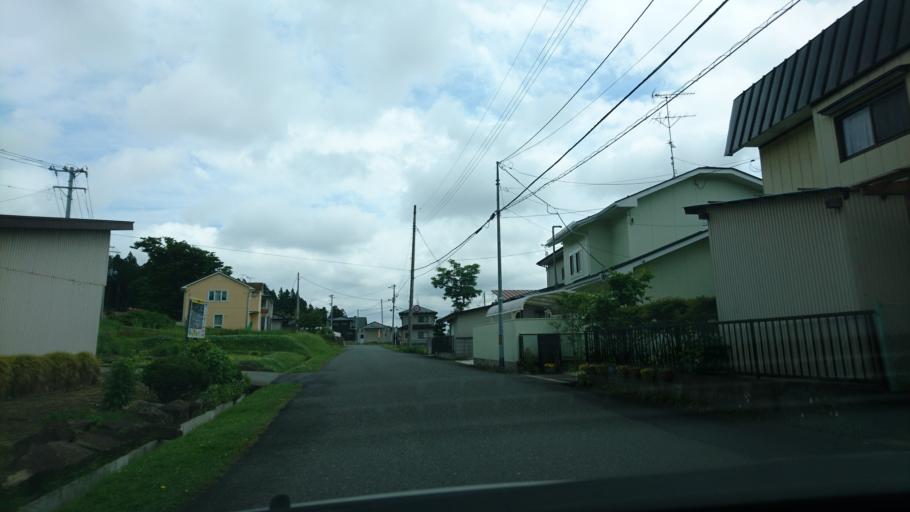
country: JP
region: Iwate
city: Ichinoseki
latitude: 38.9432
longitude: 141.0866
